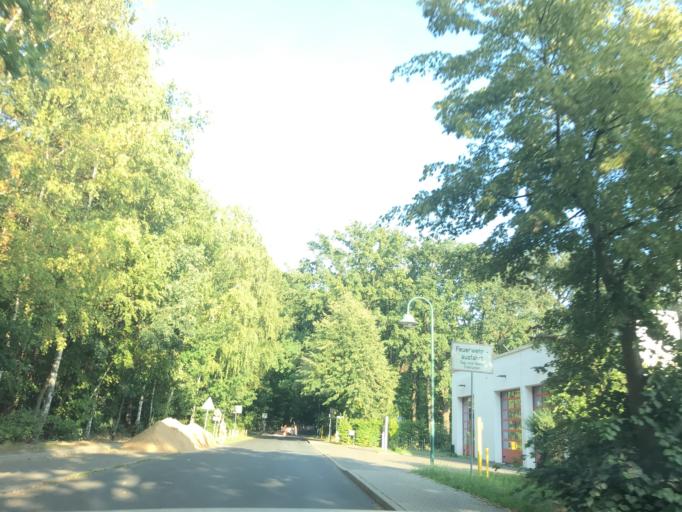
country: DE
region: Brandenburg
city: Potsdam
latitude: 52.4455
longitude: 13.0405
